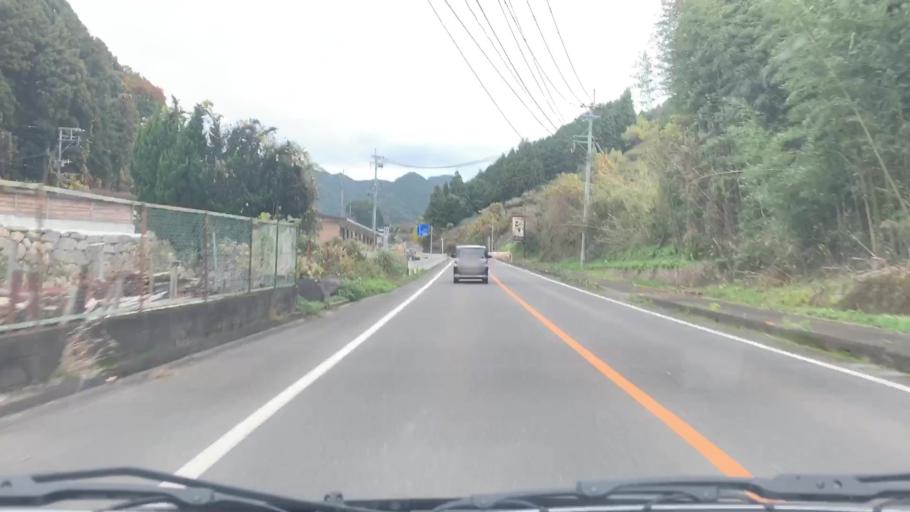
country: JP
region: Saga Prefecture
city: Ureshinomachi-shimojuku
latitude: 33.0891
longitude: 130.0108
